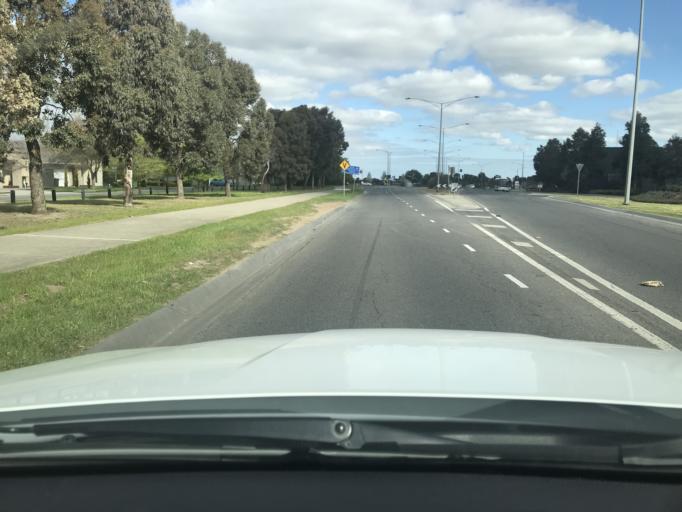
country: AU
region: Victoria
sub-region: Hume
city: Craigieburn
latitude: -37.5733
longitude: 144.9207
